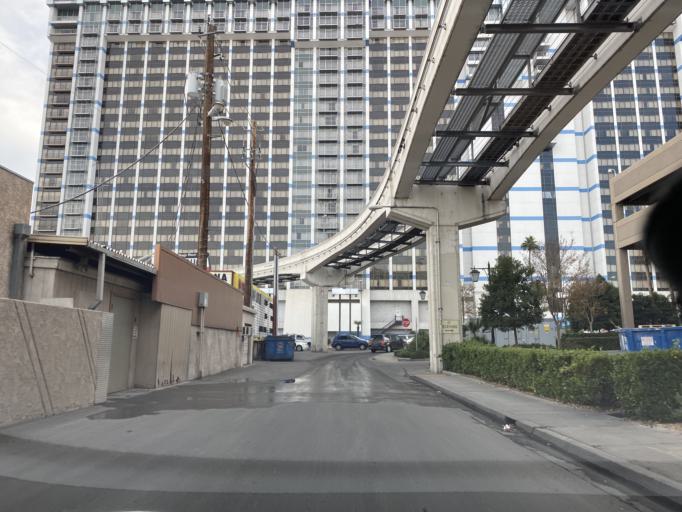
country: US
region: Nevada
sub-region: Clark County
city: Paradise
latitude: 36.1152
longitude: -115.1686
